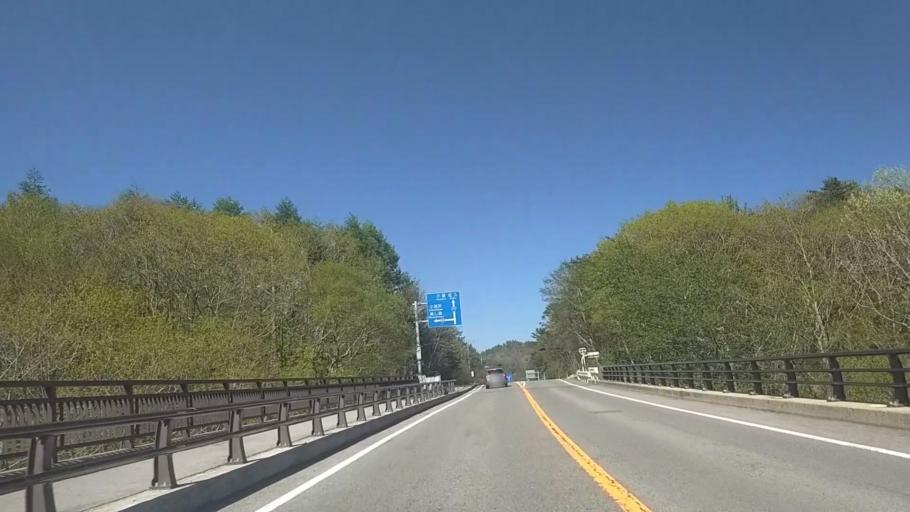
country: JP
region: Yamanashi
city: Nirasaki
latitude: 35.9302
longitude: 138.4440
